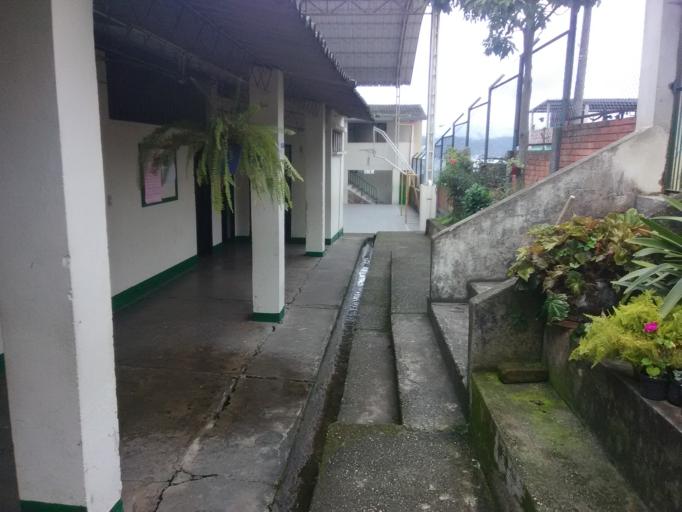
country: CO
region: Cundinamarca
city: Tenza
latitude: 5.0959
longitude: -73.4437
